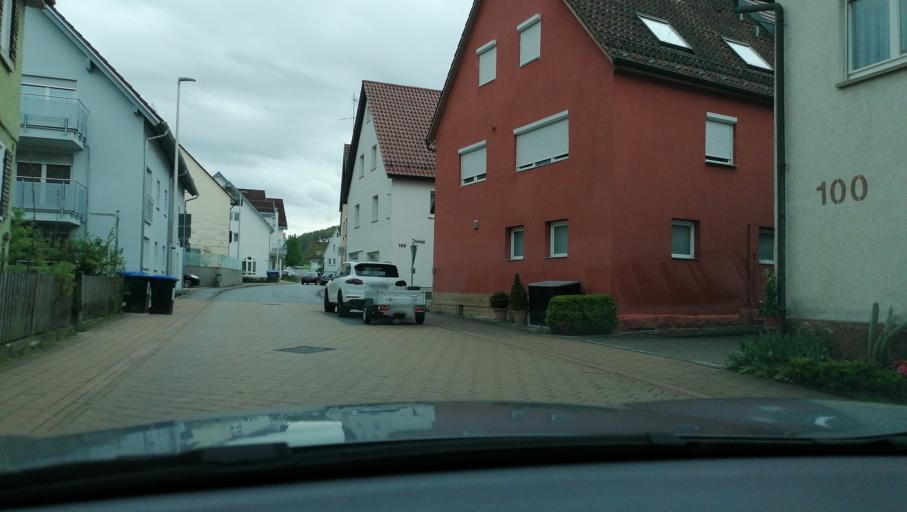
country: DE
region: Baden-Wuerttemberg
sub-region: Regierungsbezirk Stuttgart
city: Winnenden
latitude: 48.8644
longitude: 9.4310
